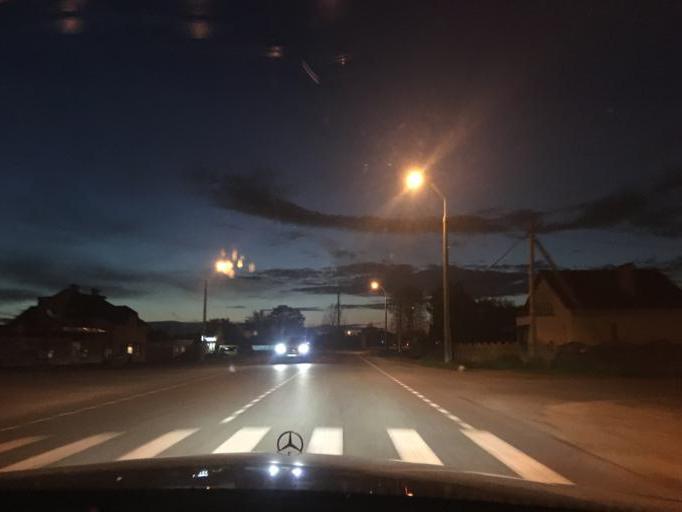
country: BY
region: Brest
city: Brest
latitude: 52.0633
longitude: 23.6913
